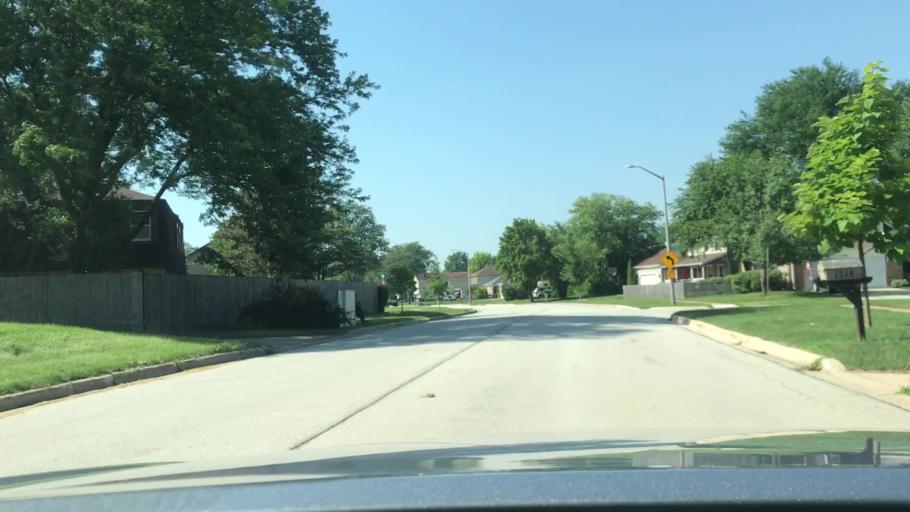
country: US
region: Illinois
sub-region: DuPage County
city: Lisle
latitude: 41.8292
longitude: -88.0842
